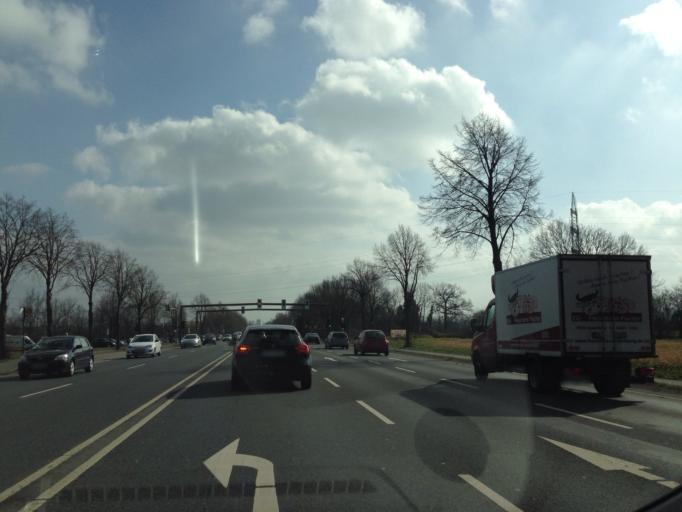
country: DE
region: North Rhine-Westphalia
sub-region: Regierungsbezirk Munster
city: Muenster
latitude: 51.9849
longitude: 7.5872
